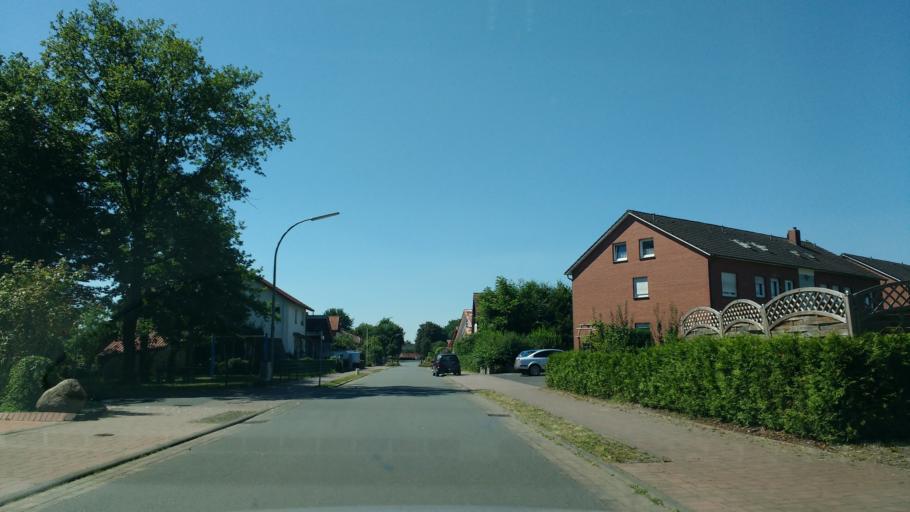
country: DE
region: North Rhine-Westphalia
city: Geseke
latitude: 51.7073
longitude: 8.4877
